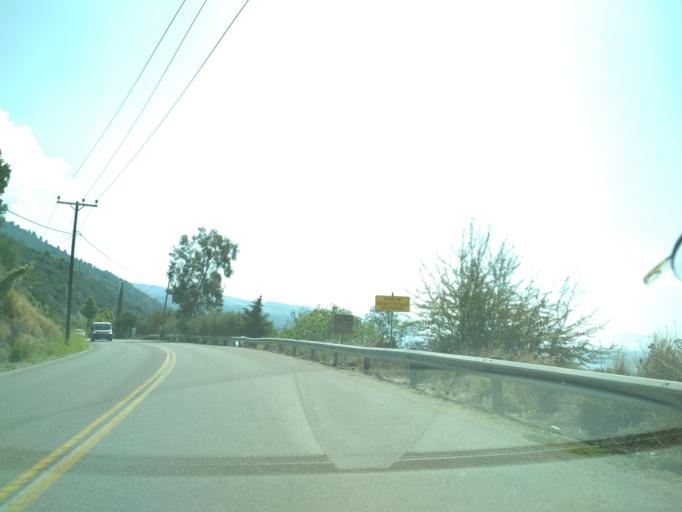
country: GR
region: Central Greece
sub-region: Nomos Evvoias
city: Roviai
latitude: 38.8380
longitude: 23.1805
